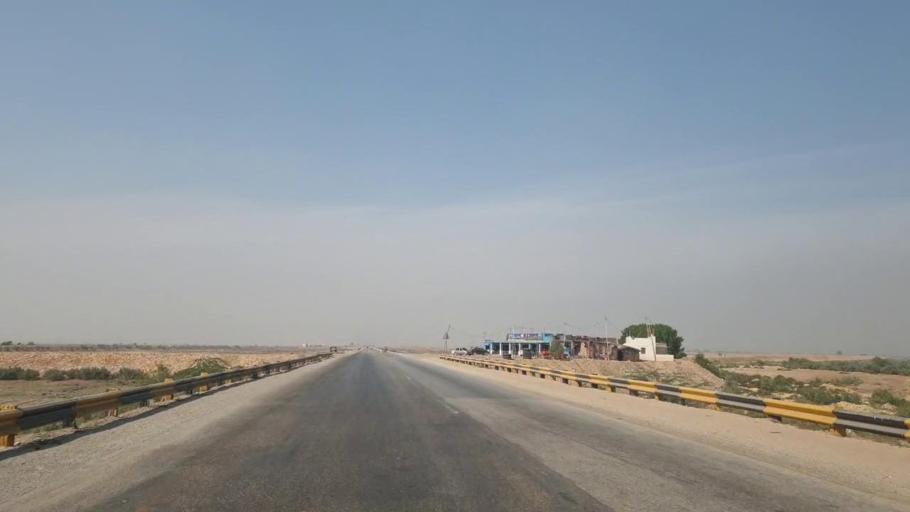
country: PK
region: Sindh
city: Hala
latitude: 25.8810
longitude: 68.2474
